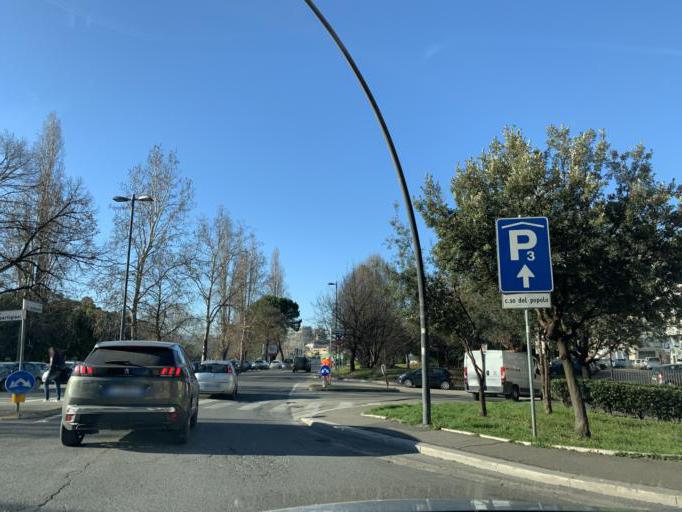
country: IT
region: Umbria
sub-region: Provincia di Terni
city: Terni
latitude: 42.5598
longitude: 12.6496
